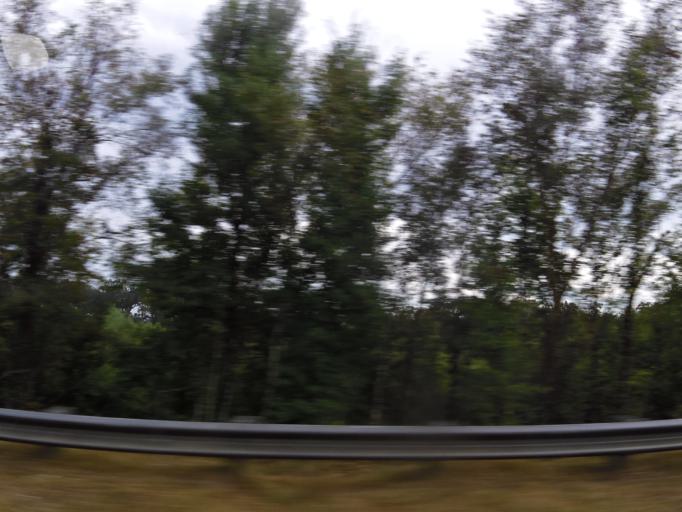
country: US
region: Georgia
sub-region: Long County
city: Ludowici
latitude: 31.6755
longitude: -81.8223
